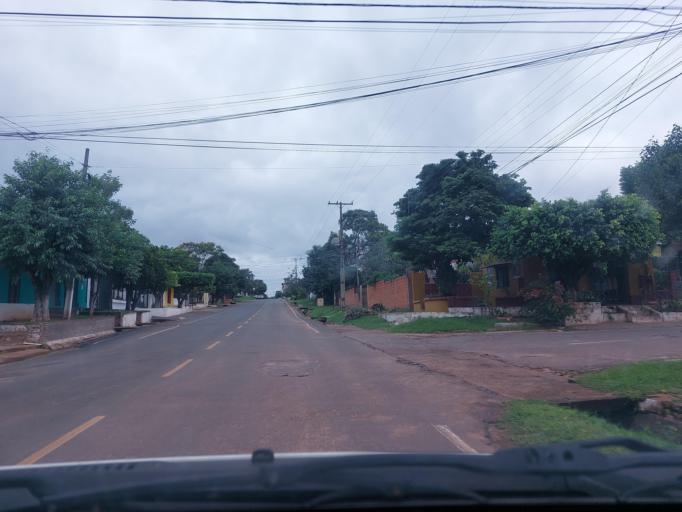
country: PY
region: San Pedro
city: Guayaybi
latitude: -24.6595
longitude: -56.4394
